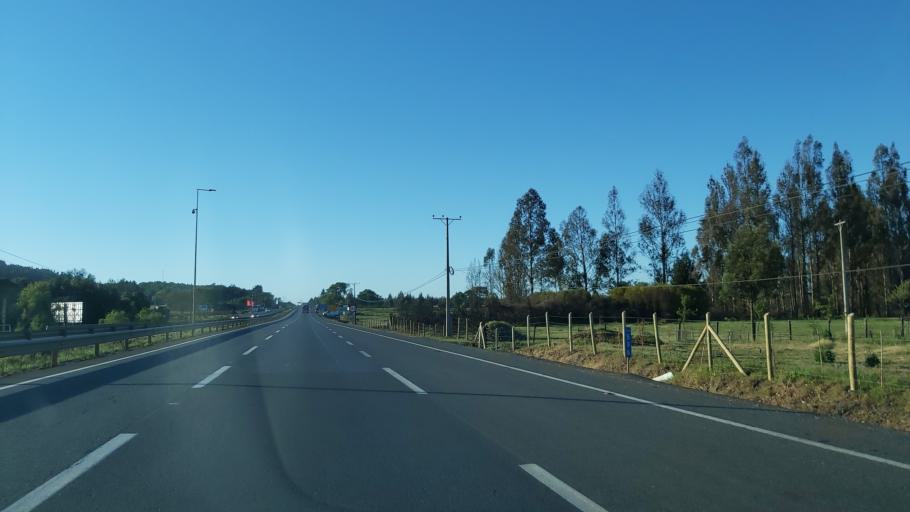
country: CL
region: Araucania
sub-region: Provincia de Malleco
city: Victoria
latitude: -38.1297
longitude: -72.3259
